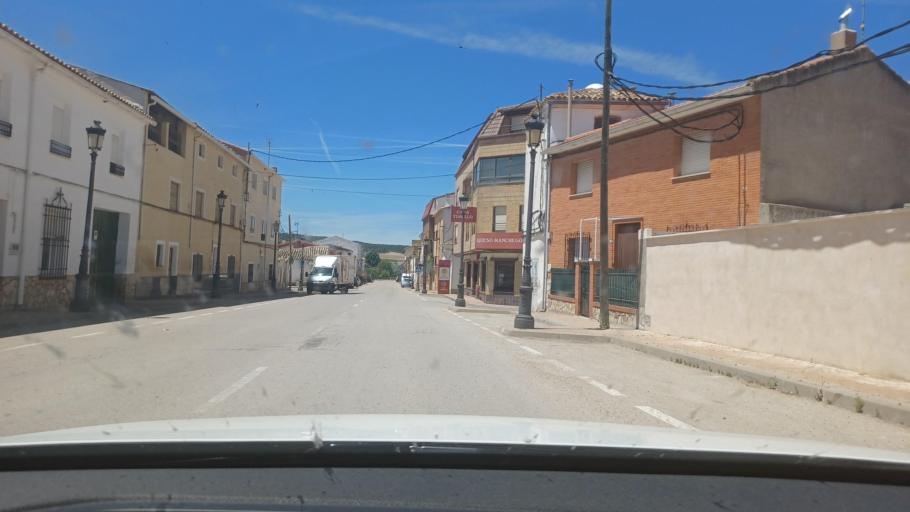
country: ES
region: Castille-La Mancha
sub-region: Provincia de Cuenca
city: Villares del Saz
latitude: 39.8393
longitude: -2.5037
